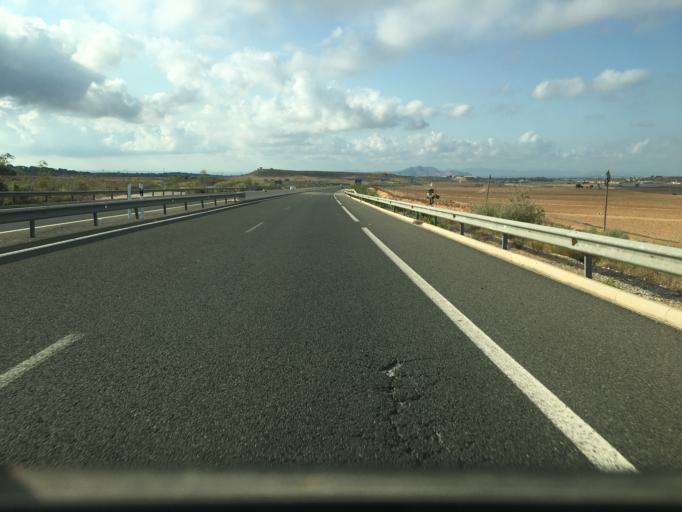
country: ES
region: Murcia
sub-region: Murcia
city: Beniel
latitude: 37.9089
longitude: -0.9562
